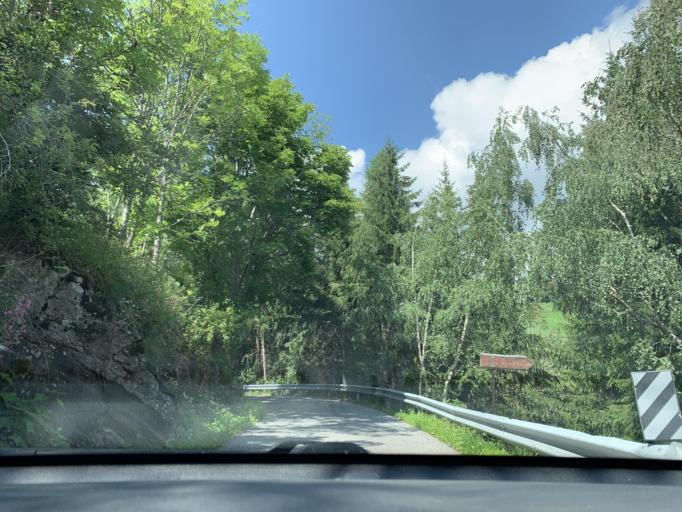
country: IT
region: Trentino-Alto Adige
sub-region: Bolzano
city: Avelengo
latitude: 46.6502
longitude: 11.2244
